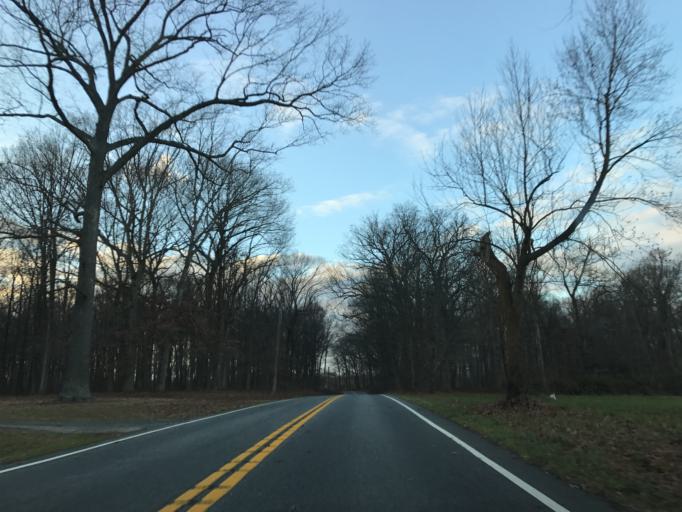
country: US
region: Pennsylvania
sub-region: York County
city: Susquehanna Trails
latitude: 39.7136
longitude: -76.2705
